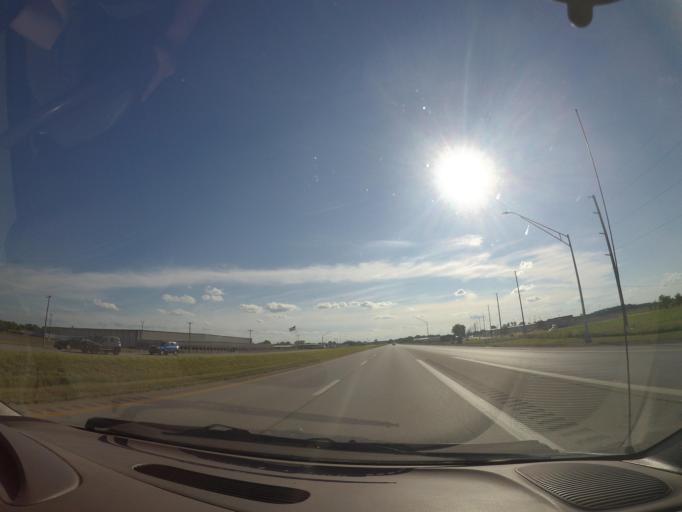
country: US
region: Ohio
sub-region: Henry County
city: Napoleon
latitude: 41.4135
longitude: -84.1103
